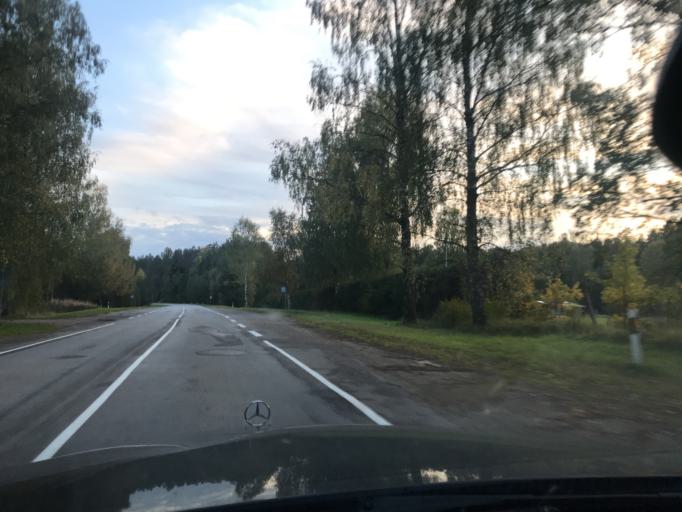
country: EE
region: Valgamaa
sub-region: Torva linn
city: Torva
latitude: 58.0051
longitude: 26.0829
